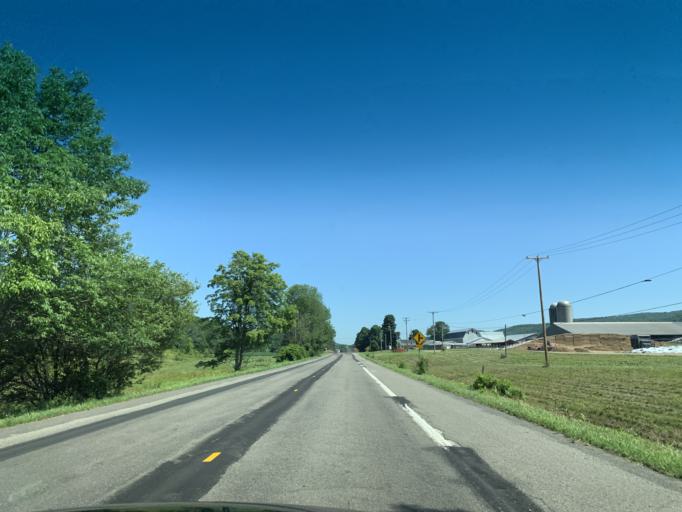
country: US
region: New York
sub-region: Delaware County
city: Sidney
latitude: 42.3525
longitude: -75.4025
